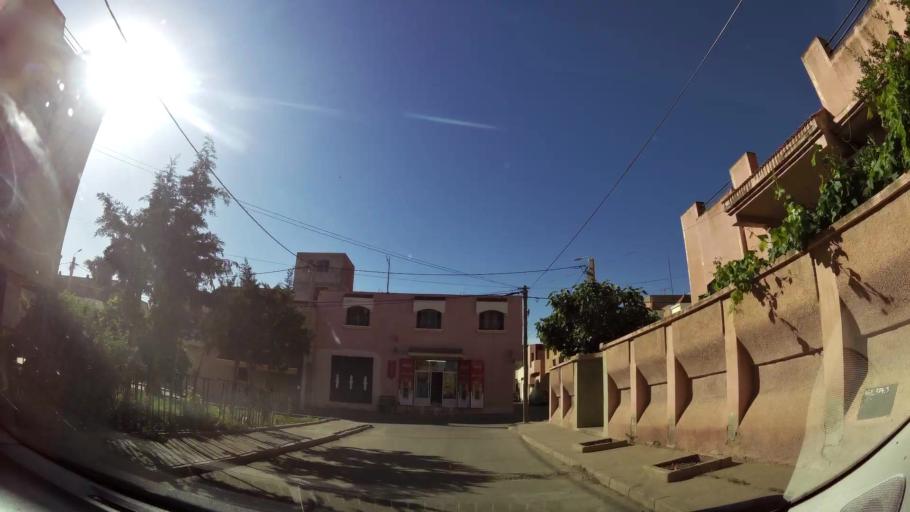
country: MA
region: Oriental
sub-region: Oujda-Angad
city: Oujda
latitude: 34.6537
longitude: -1.8969
